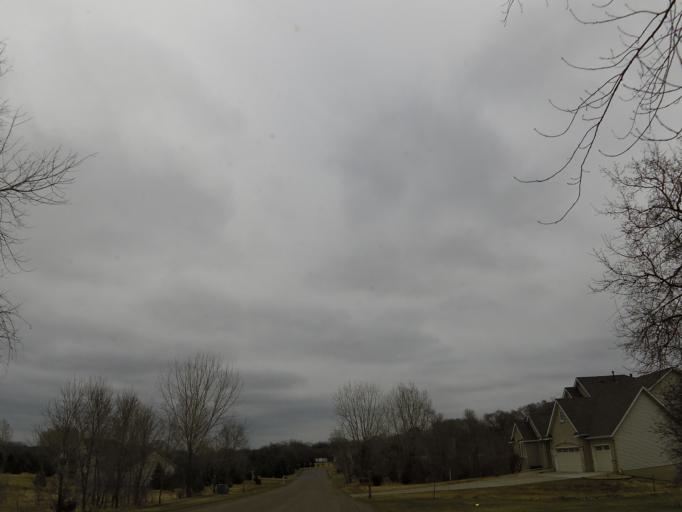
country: US
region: Minnesota
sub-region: Washington County
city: Lakeland
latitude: 44.9682
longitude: -92.8072
